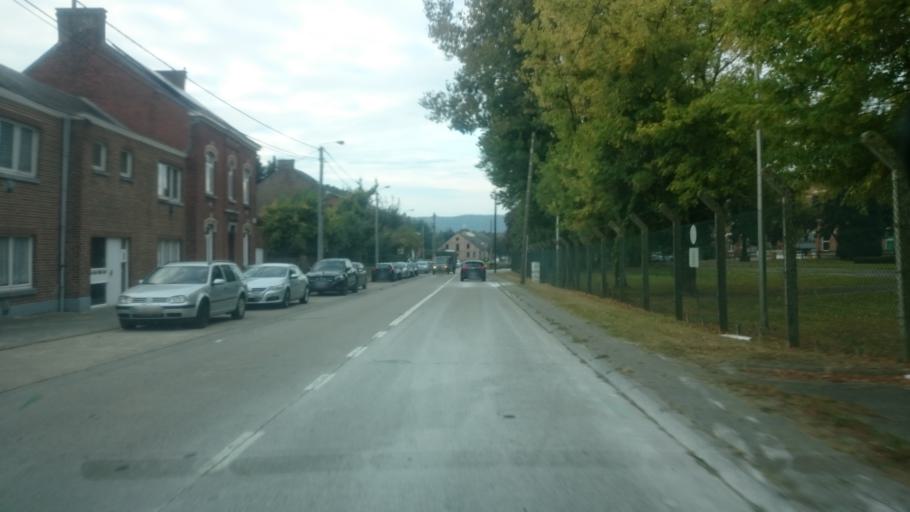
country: BE
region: Wallonia
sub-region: Province de Namur
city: Namur
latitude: 50.4668
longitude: 4.8188
